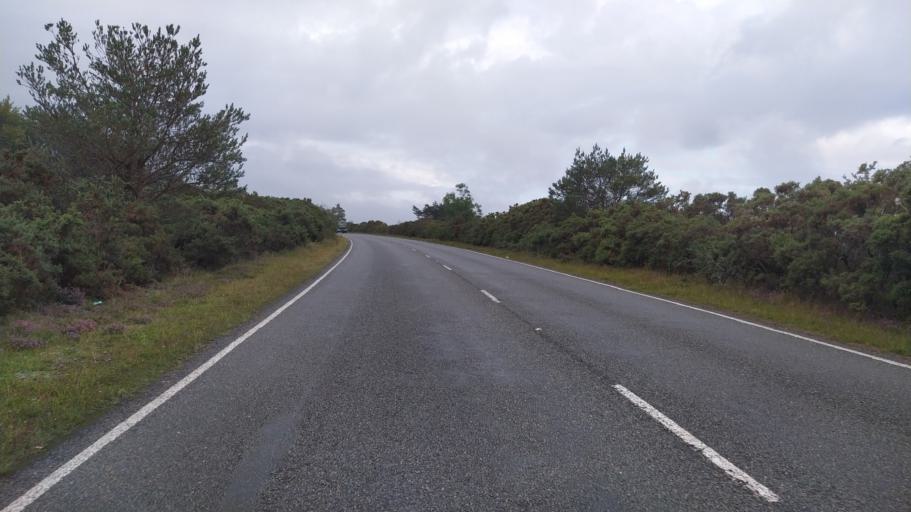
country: GB
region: England
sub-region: Hampshire
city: Sway
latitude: 50.8226
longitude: -1.6549
